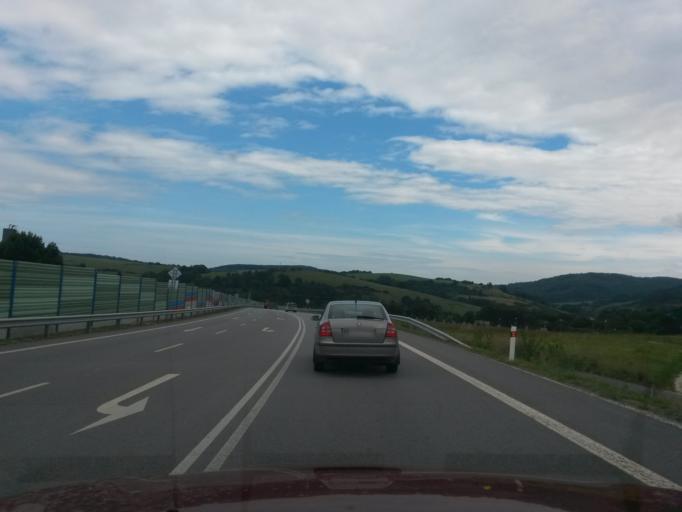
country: SK
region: Presovsky
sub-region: Okres Bardejov
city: Bardejov
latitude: 49.2842
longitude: 21.2652
